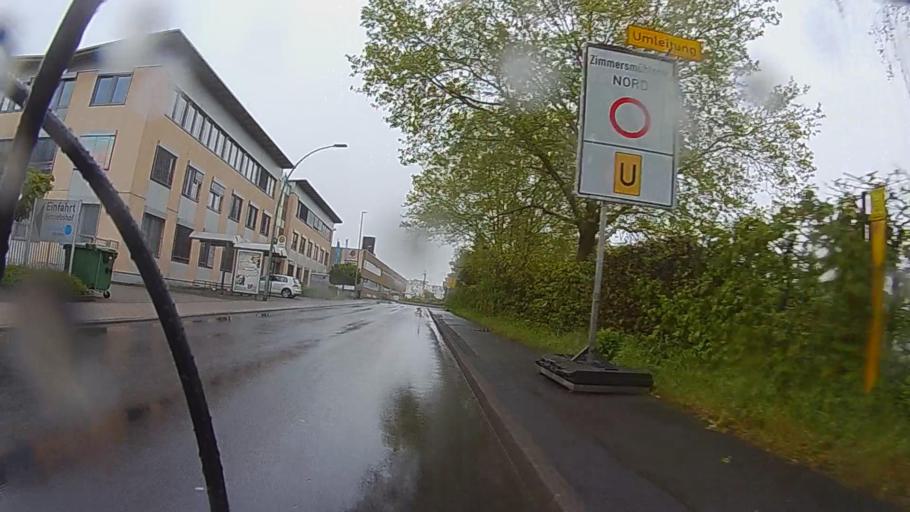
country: DE
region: Hesse
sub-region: Regierungsbezirk Darmstadt
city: Oberursel
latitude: 50.1898
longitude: 8.5919
